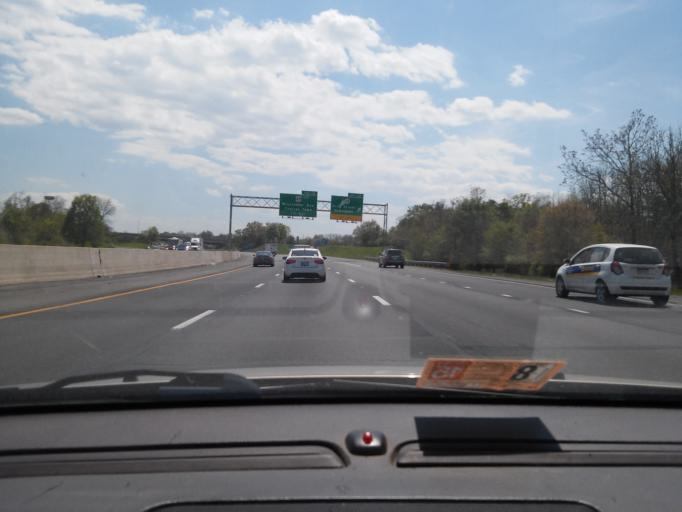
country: US
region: West Virginia
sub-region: Berkeley County
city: Martinsburg
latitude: 39.4699
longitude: -77.9895
